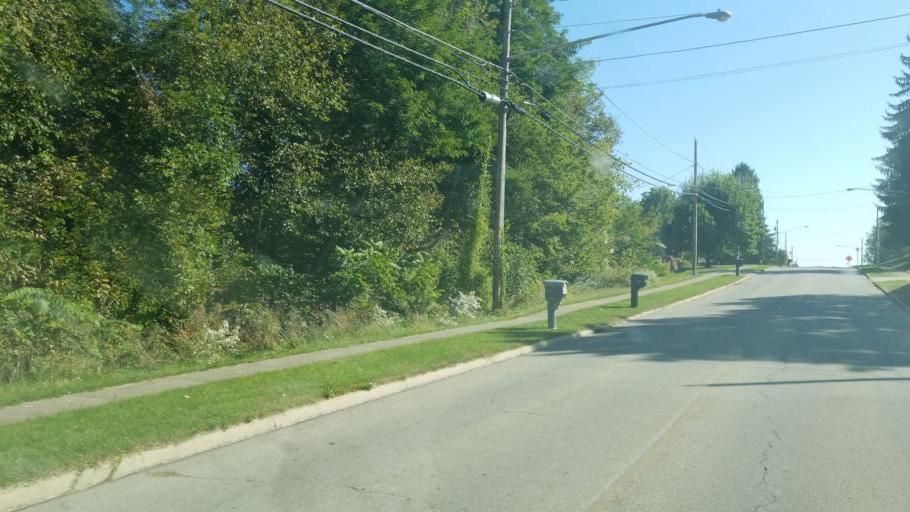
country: US
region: Ohio
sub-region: Richland County
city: Lexington
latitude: 40.6803
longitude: -82.5952
